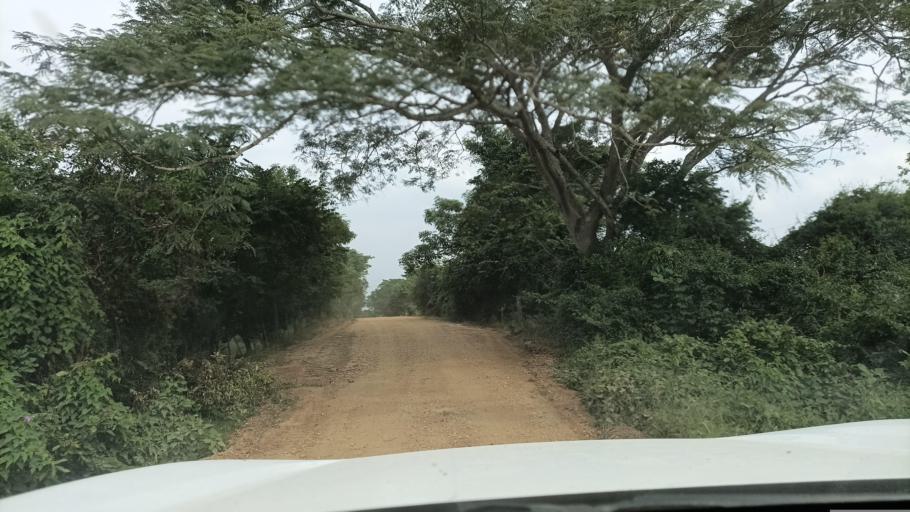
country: MX
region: Veracruz
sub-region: Texistepec
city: San Lorenzo Tenochtitlan
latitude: 17.7740
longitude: -94.8021
